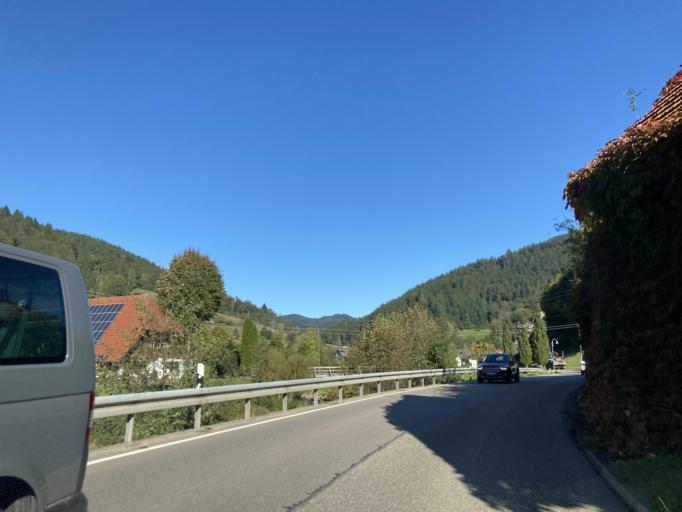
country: DE
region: Baden-Wuerttemberg
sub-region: Freiburg Region
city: Oberwolfach
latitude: 48.3405
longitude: 8.2246
